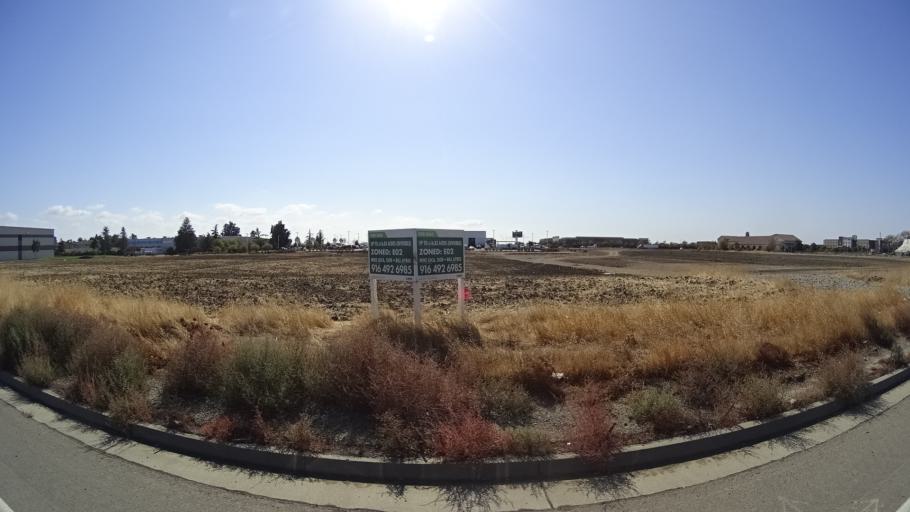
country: US
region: California
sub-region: Yolo County
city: Woodland
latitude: 38.6771
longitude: -121.7203
